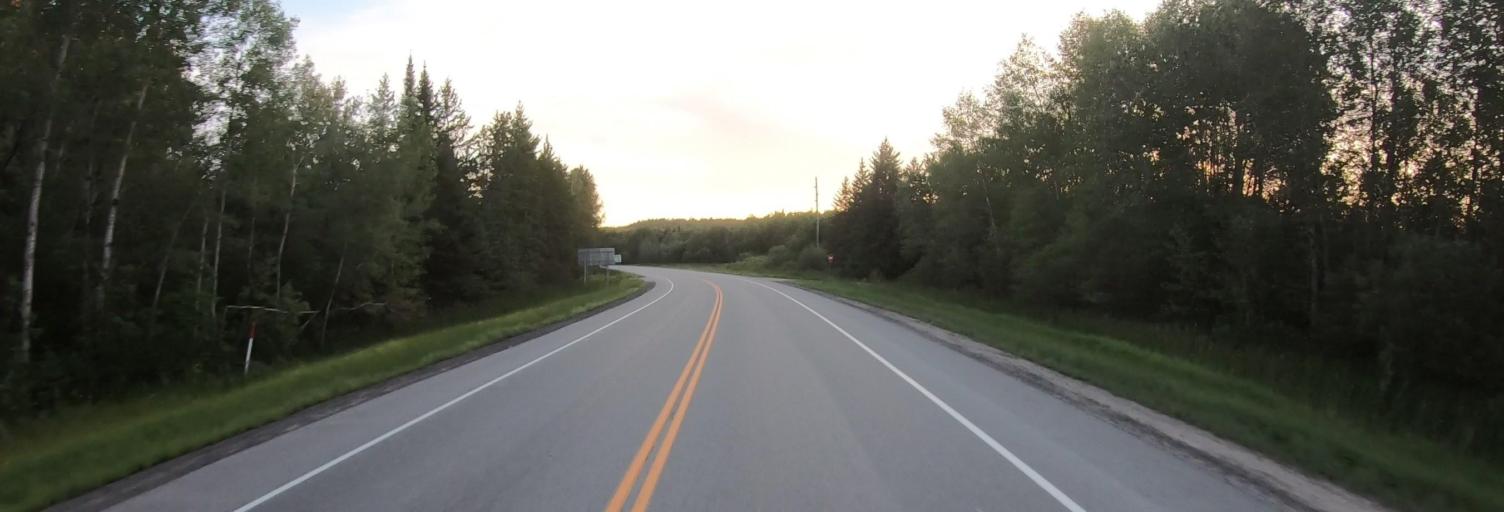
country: US
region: Minnesota
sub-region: Saint Louis County
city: Aurora
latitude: 47.8120
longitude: -92.2503
